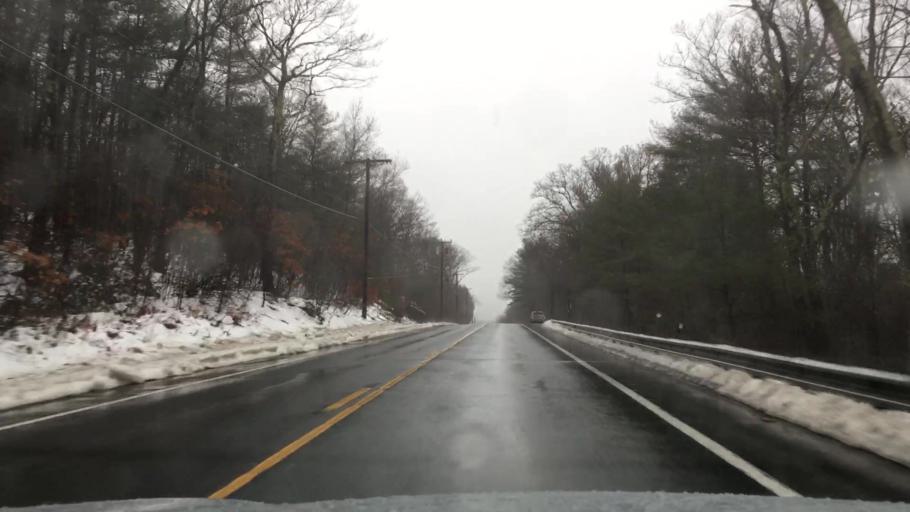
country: US
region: Massachusetts
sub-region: Hampshire County
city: Pelham
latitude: 42.3870
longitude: -72.4022
